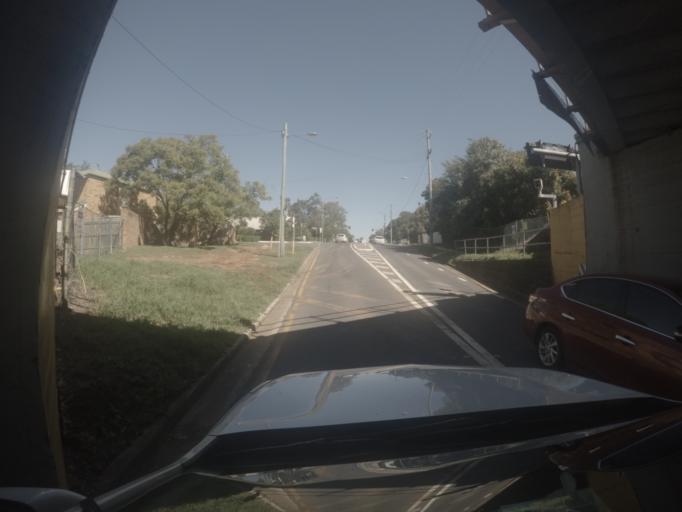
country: AU
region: Queensland
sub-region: Brisbane
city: Rocklea
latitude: -27.5368
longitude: 152.9822
